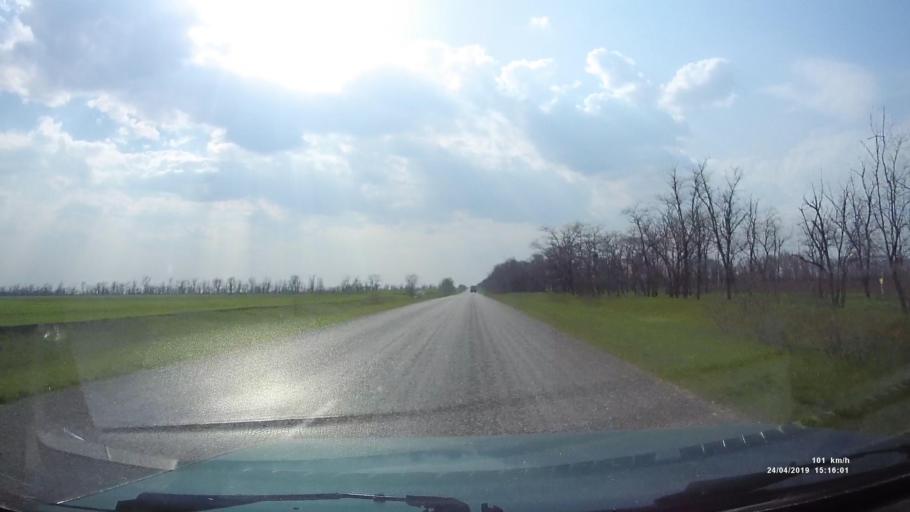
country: RU
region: Rostov
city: Remontnoye
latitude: 46.5468
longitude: 43.2228
